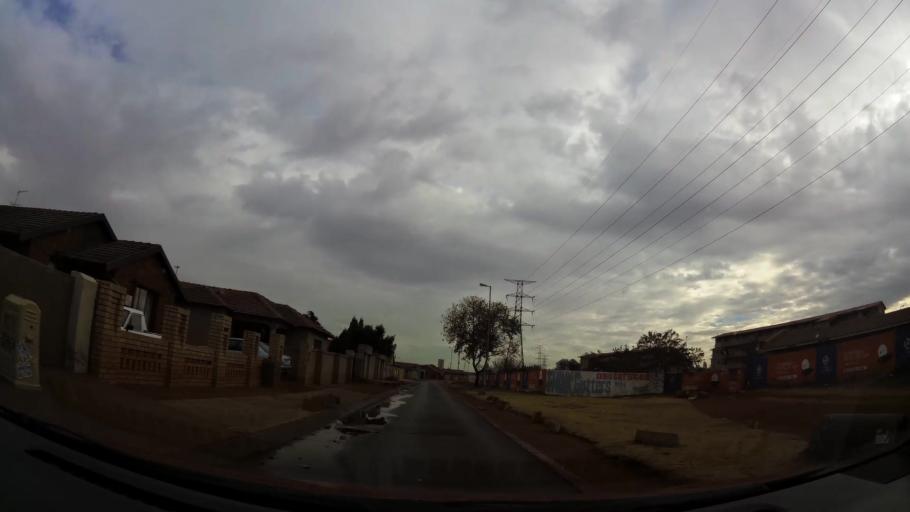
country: ZA
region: Gauteng
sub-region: City of Johannesburg Metropolitan Municipality
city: Soweto
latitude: -26.2801
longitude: 27.8442
